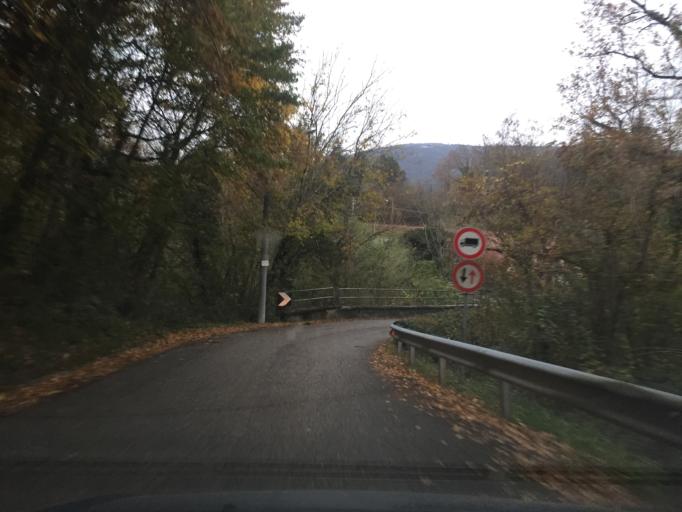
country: IT
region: Friuli Venezia Giulia
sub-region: Provincia di Gorizia
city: Gorizia
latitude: 45.9697
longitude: 13.6199
